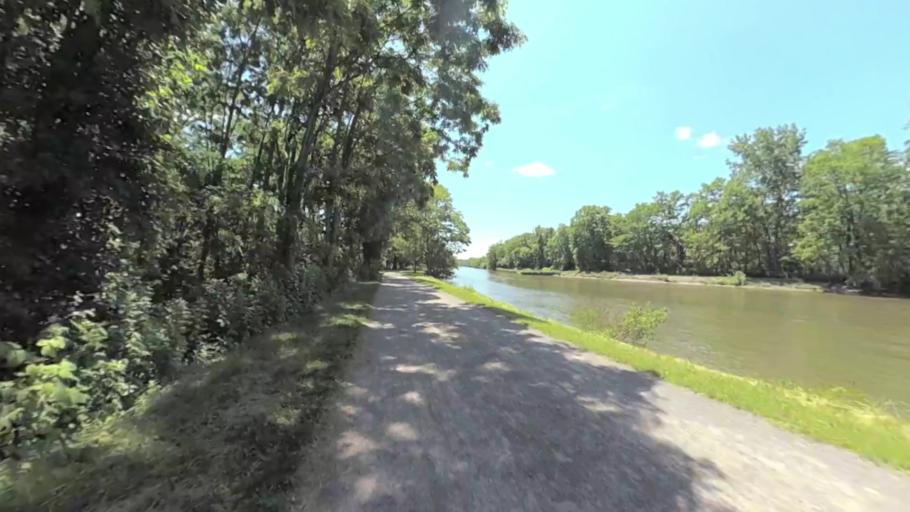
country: US
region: New York
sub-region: Monroe County
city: Pittsford
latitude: 43.0746
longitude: -77.4937
